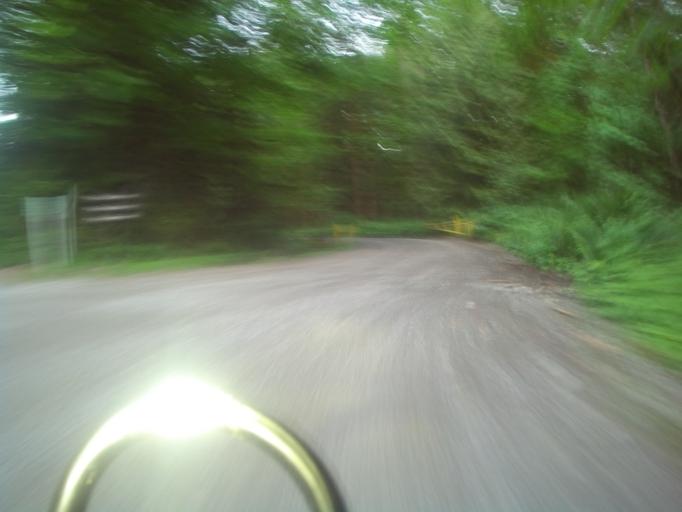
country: CA
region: British Columbia
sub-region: Fraser Valley Regional District
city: Chilliwack
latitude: 49.2959
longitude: -121.9392
